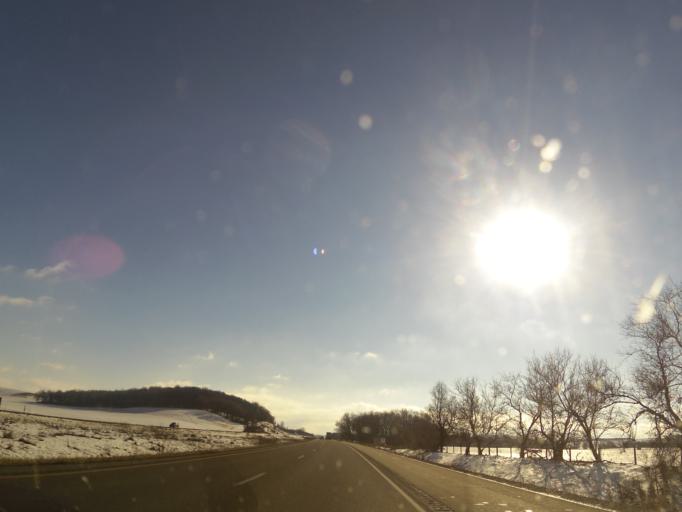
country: US
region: Wisconsin
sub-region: Eau Claire County
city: Fall Creek
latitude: 44.6939
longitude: -91.3387
